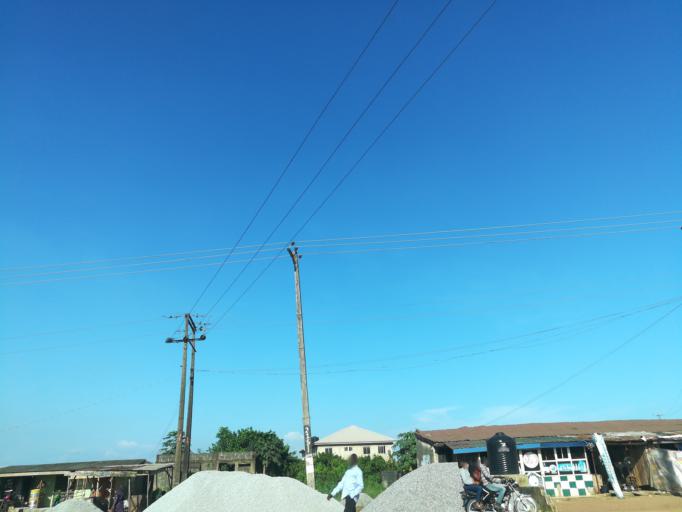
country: NG
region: Lagos
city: Ikorodu
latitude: 6.5659
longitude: 3.5345
